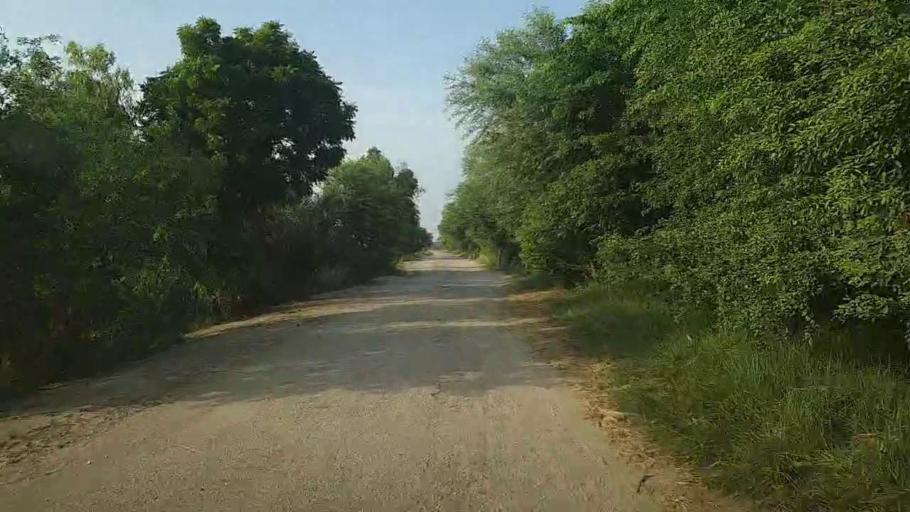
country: PK
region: Sindh
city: Ubauro
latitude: 28.3293
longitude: 69.7977
